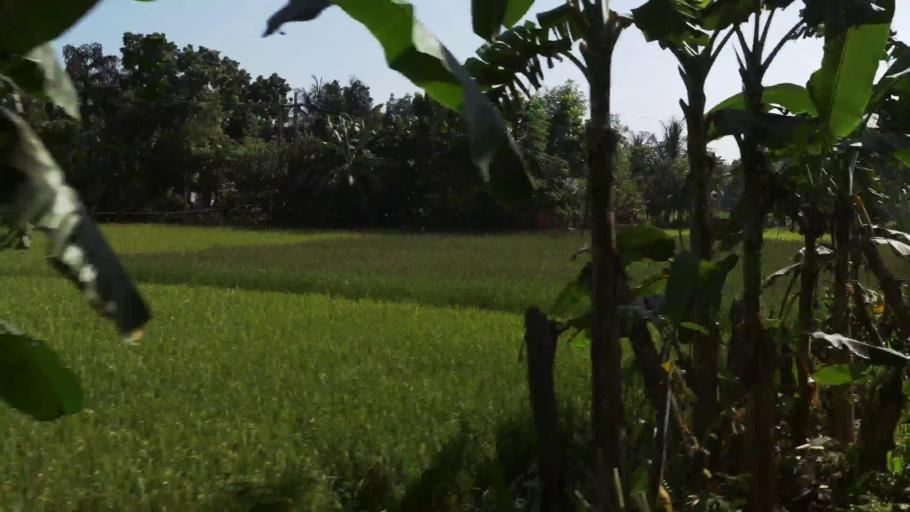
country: BD
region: Dhaka
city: Gafargaon
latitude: 24.5431
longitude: 90.5085
